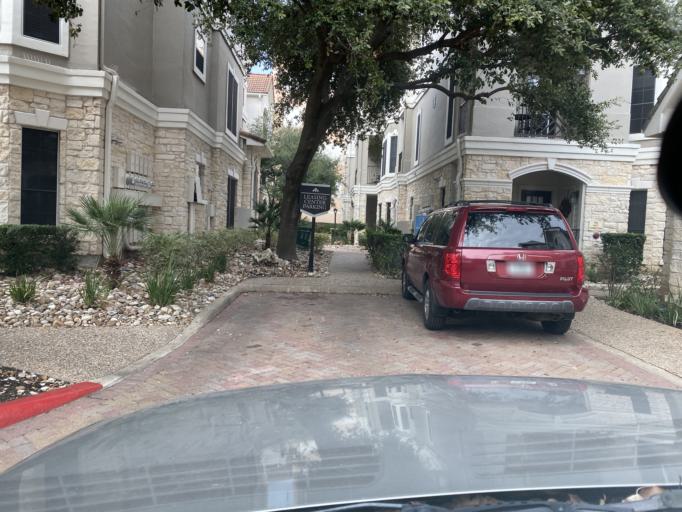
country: US
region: Texas
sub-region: Travis County
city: Austin
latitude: 30.3048
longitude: -97.7396
